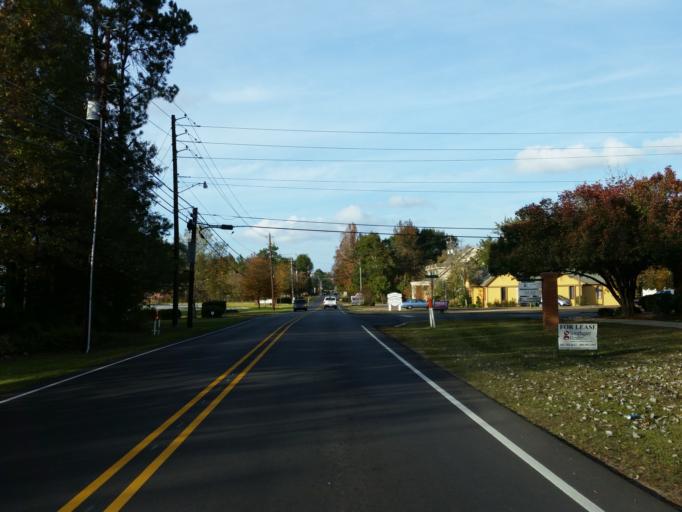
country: US
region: Mississippi
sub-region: Lamar County
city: West Hattiesburg
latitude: 31.2987
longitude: -89.3312
